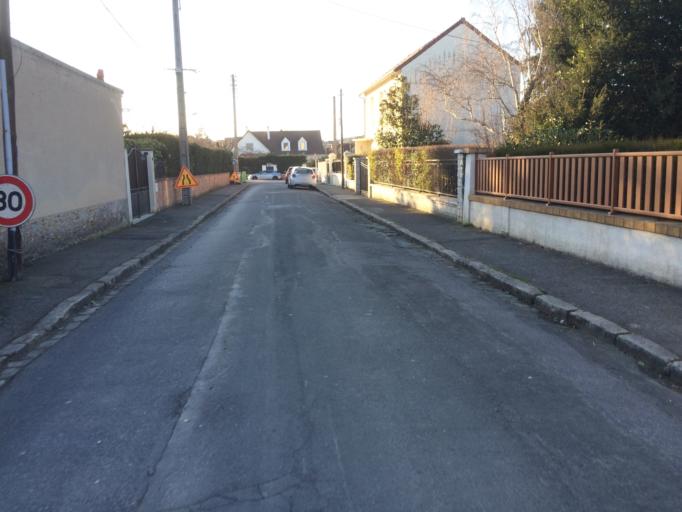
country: FR
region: Ile-de-France
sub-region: Departement de l'Essonne
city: Igny
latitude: 48.7324
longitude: 2.2201
